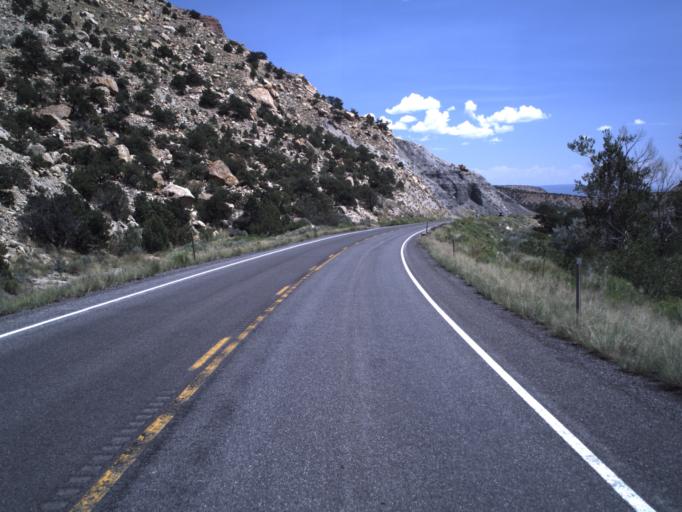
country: US
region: Utah
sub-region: Emery County
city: Huntington
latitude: 39.3927
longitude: -111.0955
